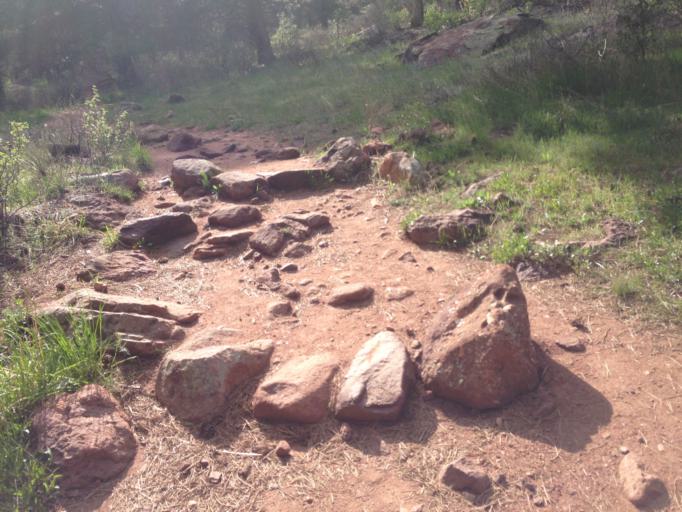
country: US
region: Colorado
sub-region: Boulder County
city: Boulder
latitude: 39.9415
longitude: -105.2691
